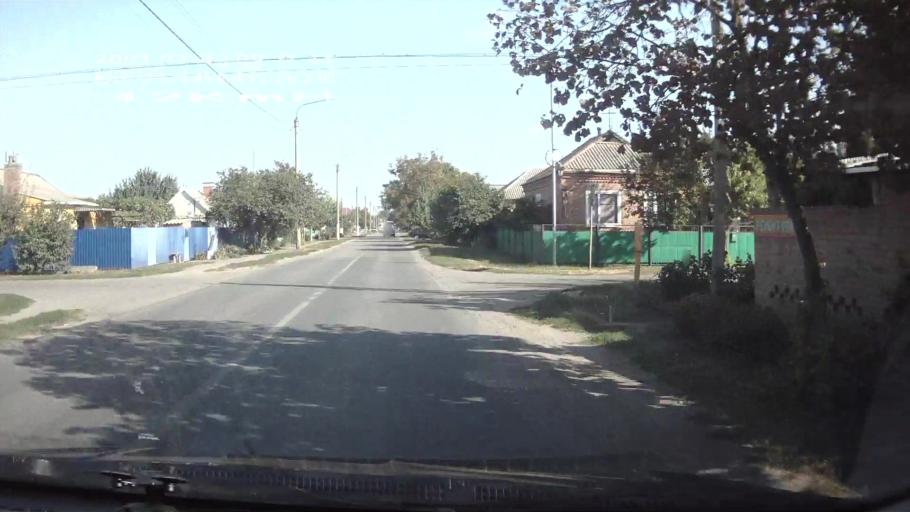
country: RU
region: Rostov
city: Tselina
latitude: 46.5316
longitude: 41.0262
